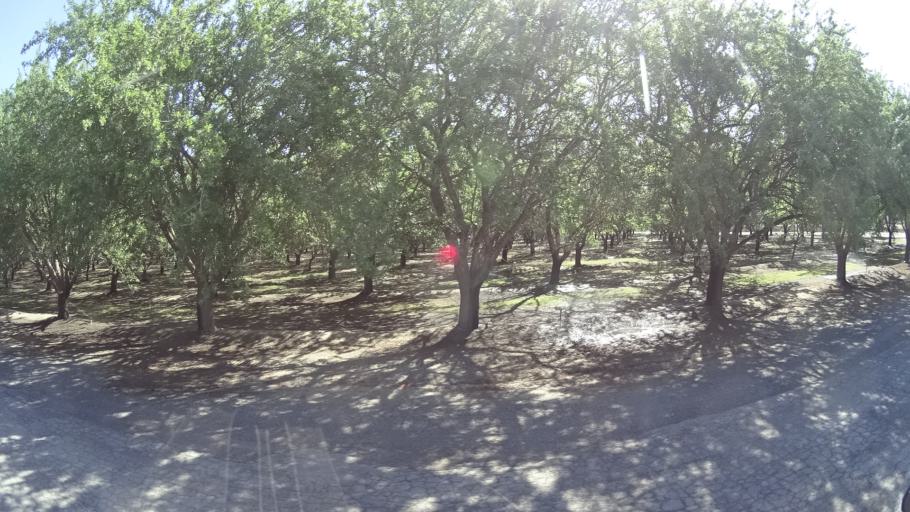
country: US
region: California
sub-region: Glenn County
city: Hamilton City
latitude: 39.7398
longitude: -122.0573
